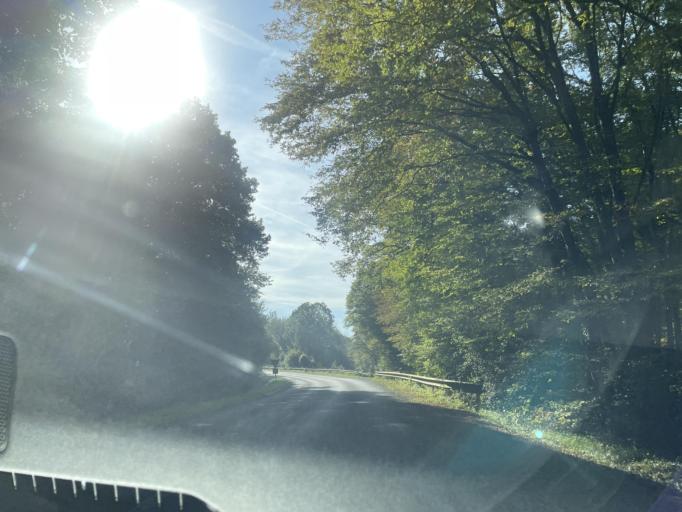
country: FR
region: Ile-de-France
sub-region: Departement de Seine-et-Marne
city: Trilport
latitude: 48.9580
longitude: 2.9845
